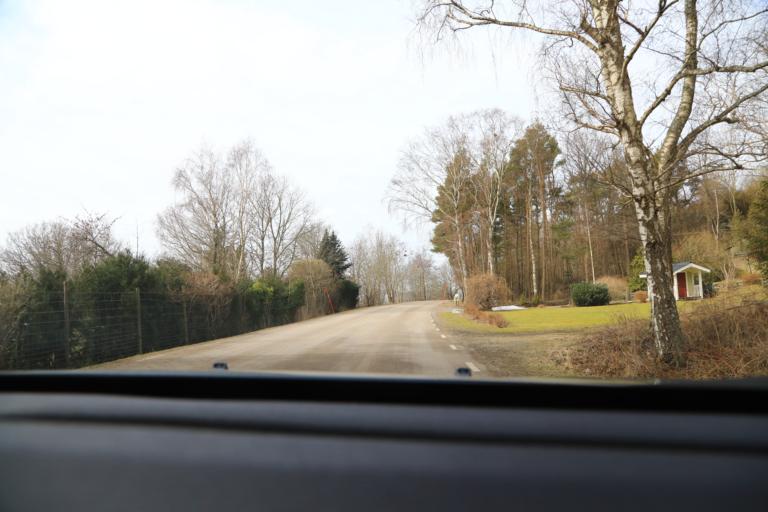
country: SE
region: Halland
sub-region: Kungsbacka Kommun
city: Frillesas
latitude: 57.2320
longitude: 12.2150
